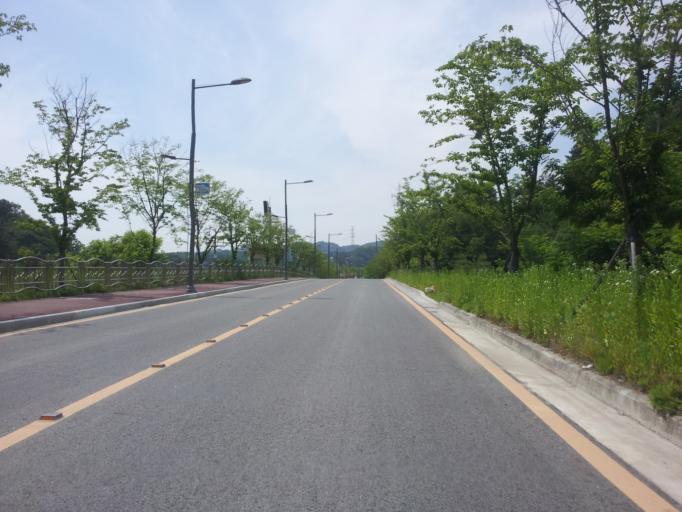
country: KR
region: Daejeon
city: Sintansin
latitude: 36.4571
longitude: 127.4691
